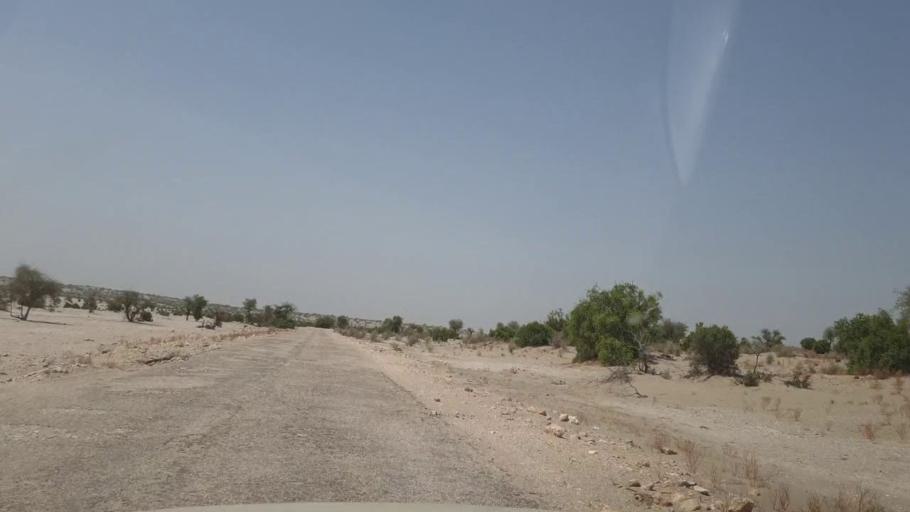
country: PK
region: Sindh
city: Khanpur
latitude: 27.3410
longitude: 69.3159
